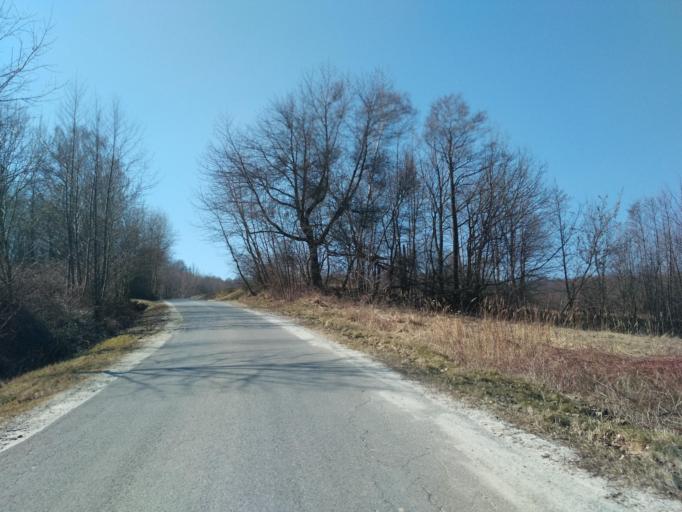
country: PL
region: Subcarpathian Voivodeship
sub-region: Powiat strzyzowski
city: Czudec
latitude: 49.9739
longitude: 21.8523
